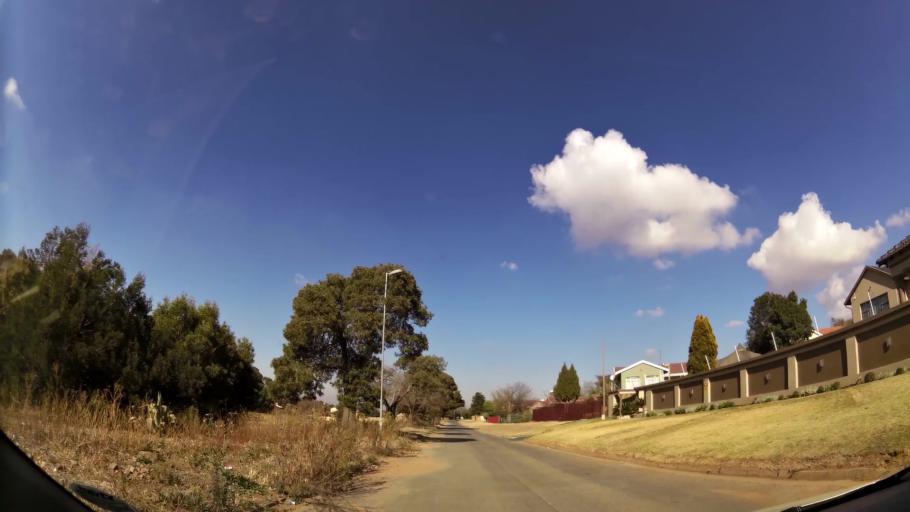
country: ZA
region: Gauteng
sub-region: City of Johannesburg Metropolitan Municipality
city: Roodepoort
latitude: -26.1377
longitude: 27.8214
